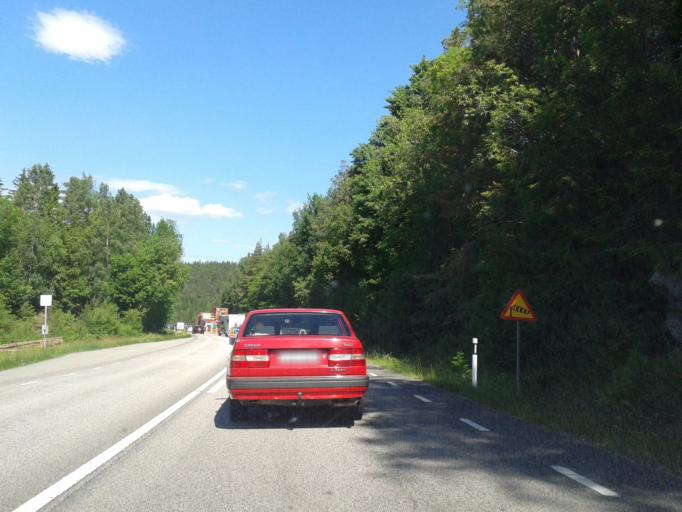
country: SE
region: Vaestra Goetaland
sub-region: Orust
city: Henan
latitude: 58.2914
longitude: 11.7043
